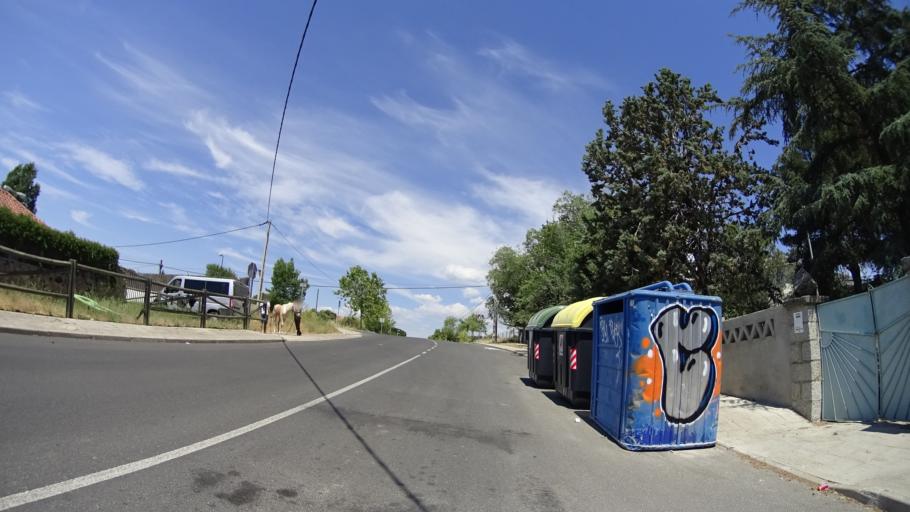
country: ES
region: Madrid
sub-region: Provincia de Madrid
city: Colmenarejo
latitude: 40.5528
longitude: -4.0064
